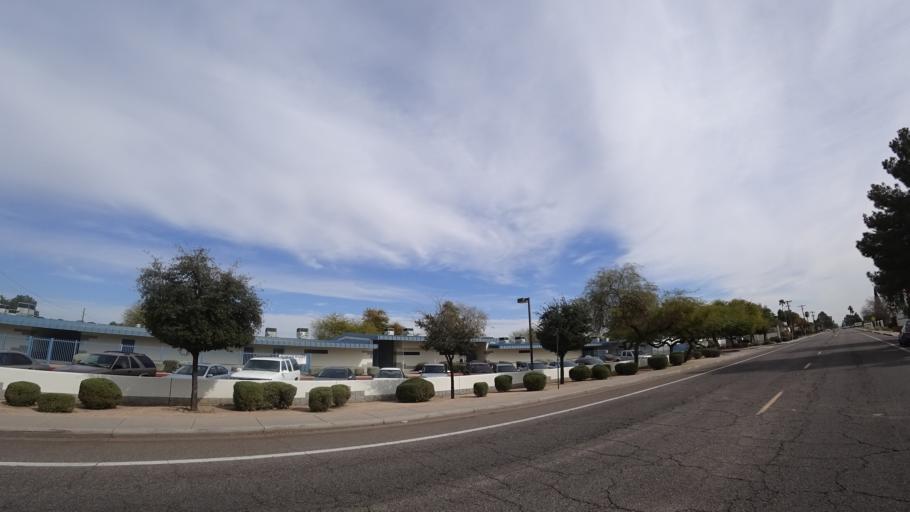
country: US
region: Arizona
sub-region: Maricopa County
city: Glendale
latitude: 33.5312
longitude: -112.1552
